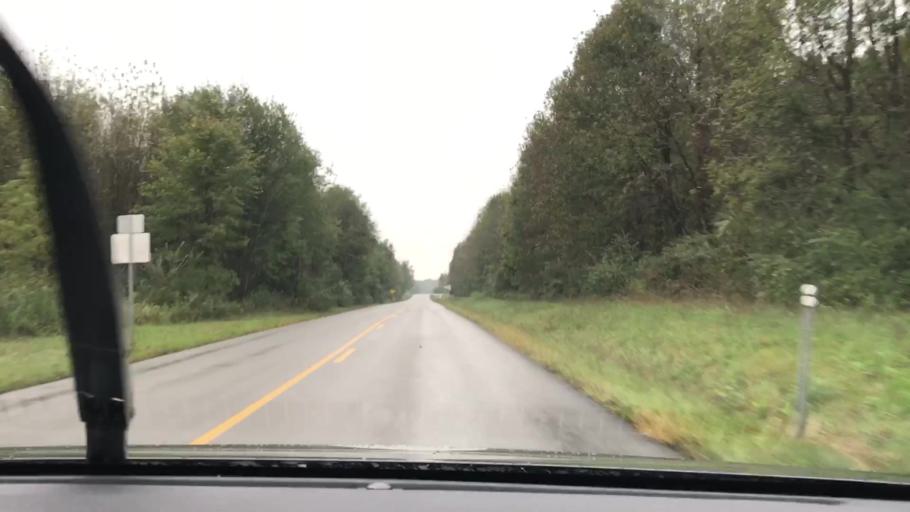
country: US
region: Kentucky
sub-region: Hopkins County
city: Madisonville
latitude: 37.3616
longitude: -87.3766
